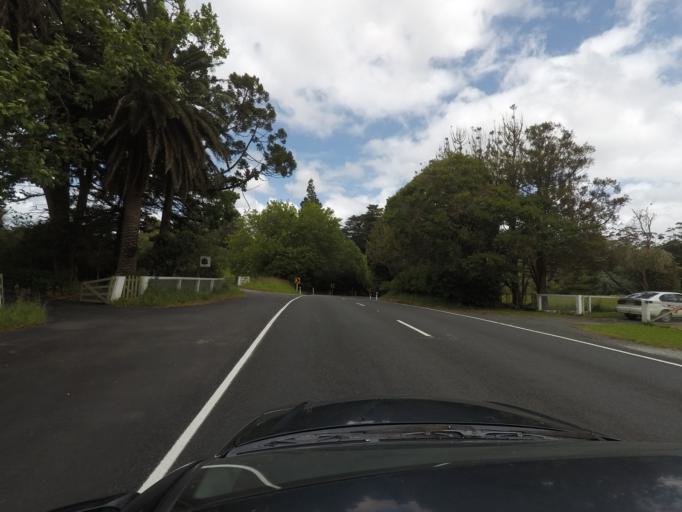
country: NZ
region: Auckland
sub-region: Auckland
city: Warkworth
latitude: -36.4847
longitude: 174.5322
